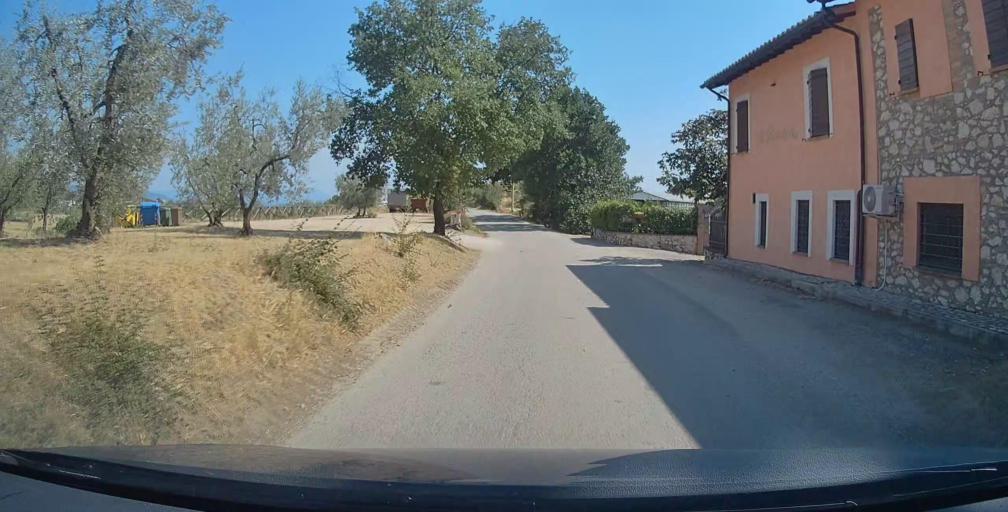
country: IT
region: Umbria
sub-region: Provincia di Terni
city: Calvi dell'Umbria
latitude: 42.3866
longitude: 12.5679
